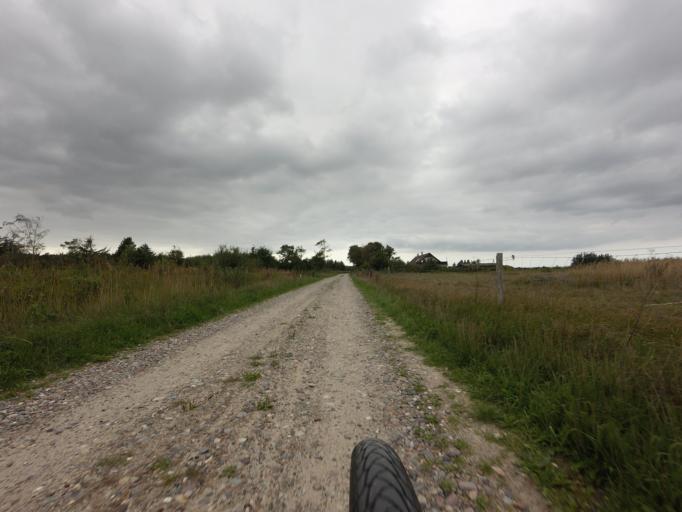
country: DK
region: North Denmark
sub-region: Hjorring Kommune
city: Hirtshals
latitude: 57.5842
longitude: 10.0472
